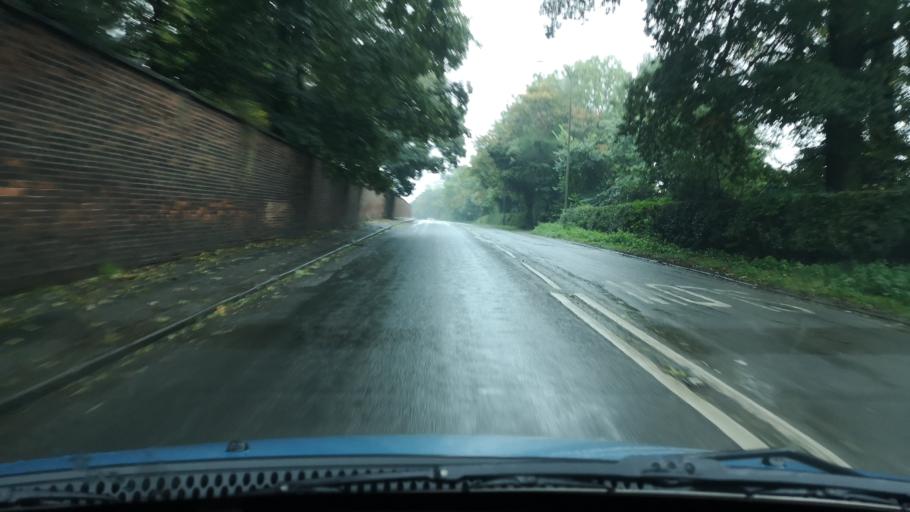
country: GB
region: England
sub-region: City and Borough of Wakefield
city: Fitzwilliam
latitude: 53.6509
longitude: -1.3910
